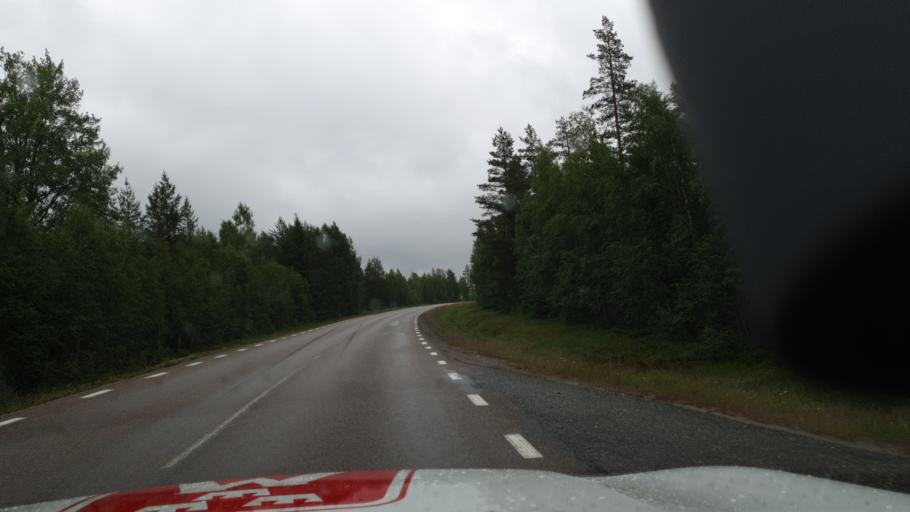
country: SE
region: Vaesterbotten
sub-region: Vannas Kommun
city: Vaennaes
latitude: 63.7945
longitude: 19.7823
